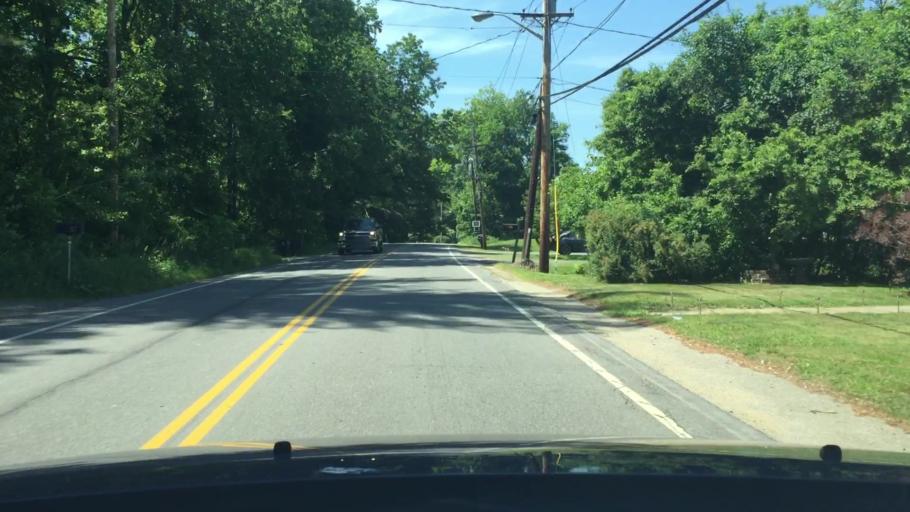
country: US
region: New Hampshire
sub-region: Rockingham County
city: Plaistow
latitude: 42.8129
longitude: -71.0921
